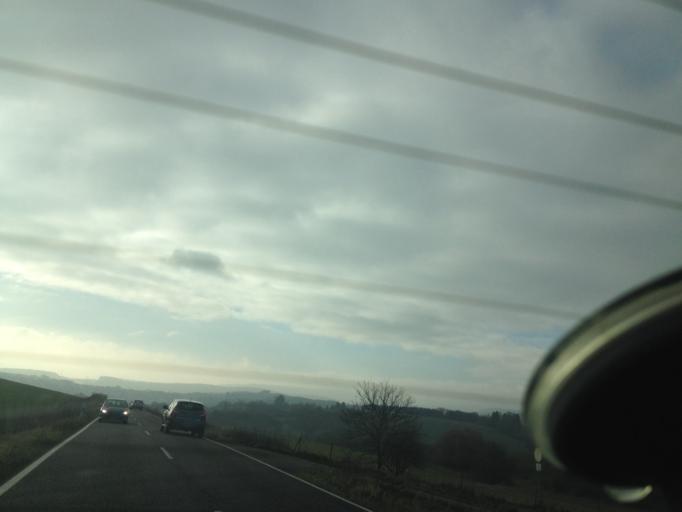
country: DE
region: Rheinland-Pfalz
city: Brucken
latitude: 49.4459
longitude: 7.3745
